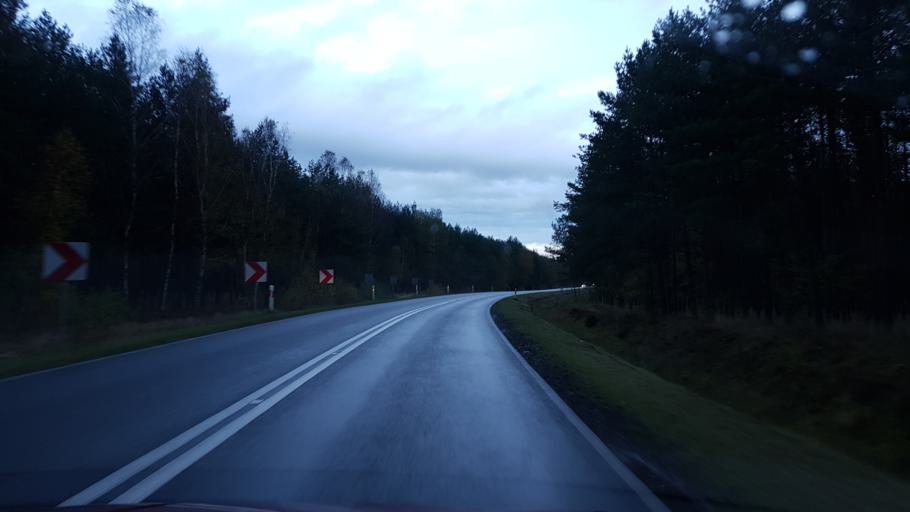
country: PL
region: Greater Poland Voivodeship
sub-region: Powiat pilski
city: Pila
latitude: 53.1885
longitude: 16.8136
